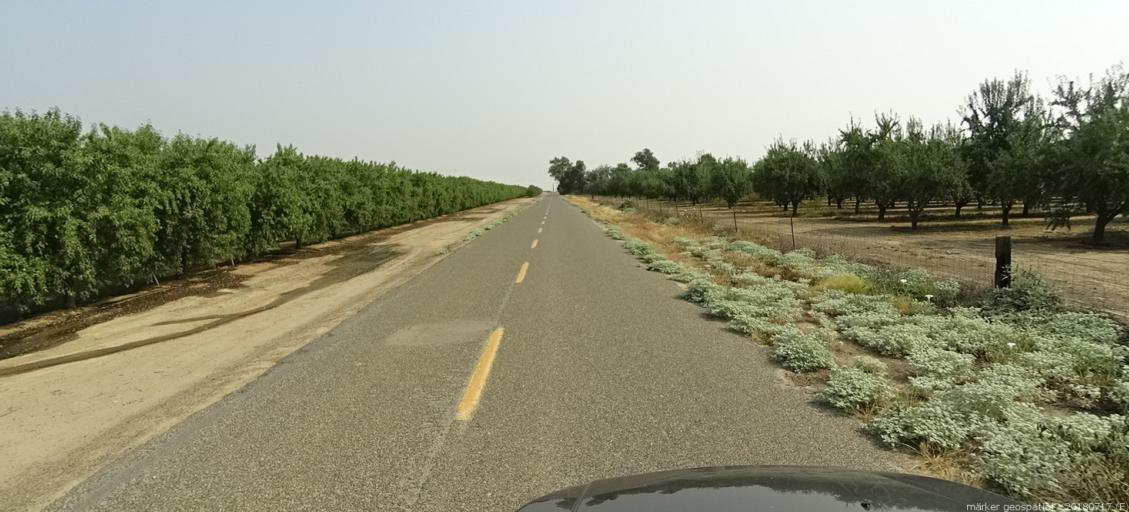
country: US
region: California
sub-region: Madera County
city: Fairmead
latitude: 37.1212
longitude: -120.1112
